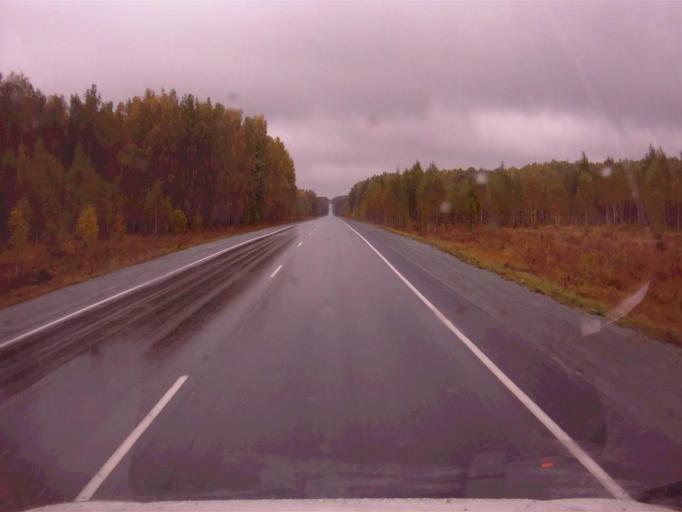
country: RU
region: Chelyabinsk
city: Tayginka
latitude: 55.5094
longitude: 60.6379
